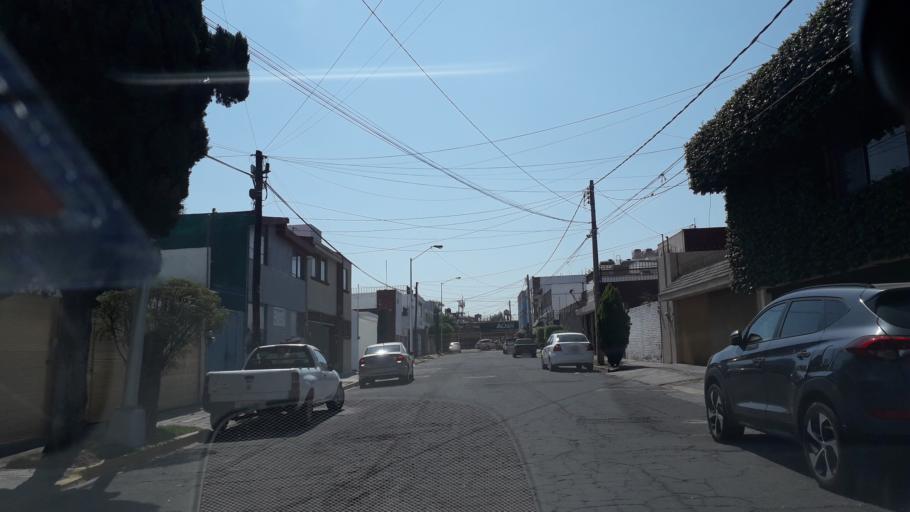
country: MX
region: Puebla
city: Puebla
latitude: 19.0194
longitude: -98.1934
